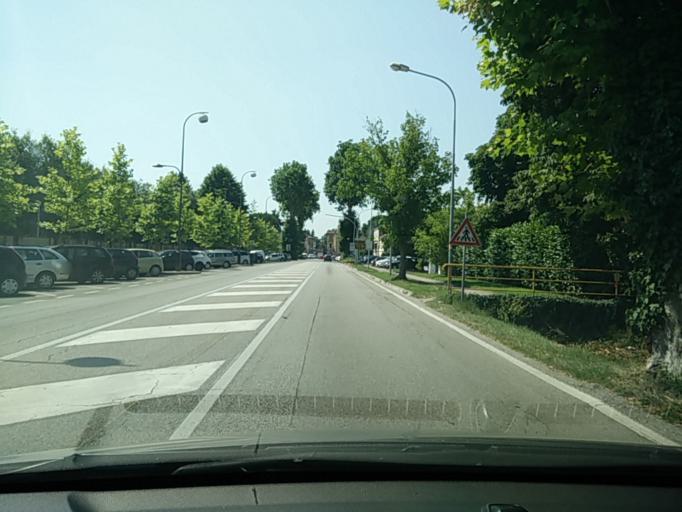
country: IT
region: Veneto
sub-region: Provincia di Treviso
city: Mogliano Veneto
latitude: 45.5639
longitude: 12.2351
